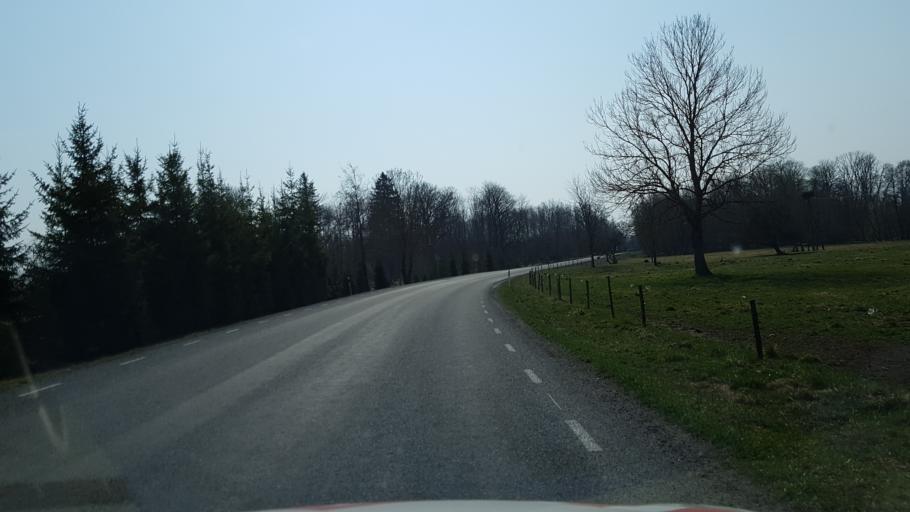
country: EE
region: Raplamaa
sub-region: Kehtna vald
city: Kehtna
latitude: 59.0257
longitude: 24.9262
